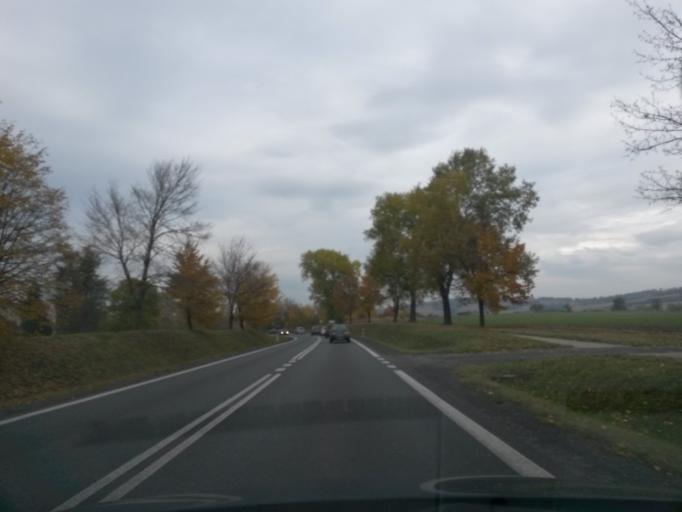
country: PL
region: Lower Silesian Voivodeship
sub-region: Powiat dzierzoniowski
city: Niemcza
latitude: 50.6919
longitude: 16.8218
